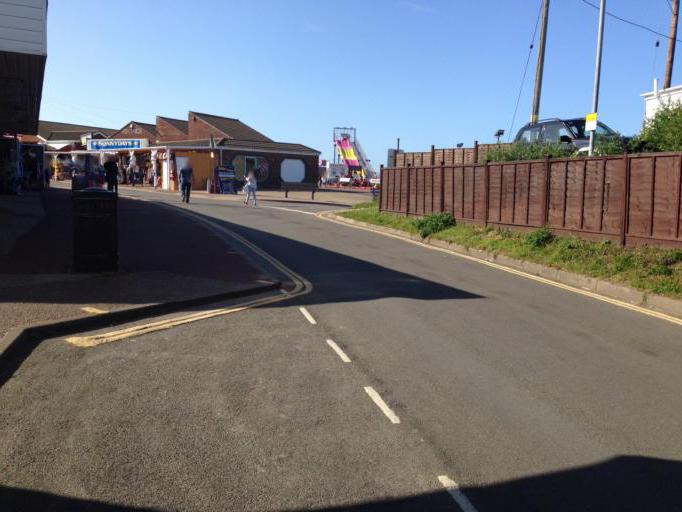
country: GB
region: England
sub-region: Norfolk
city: Hemsby
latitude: 52.6954
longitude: 1.7072
